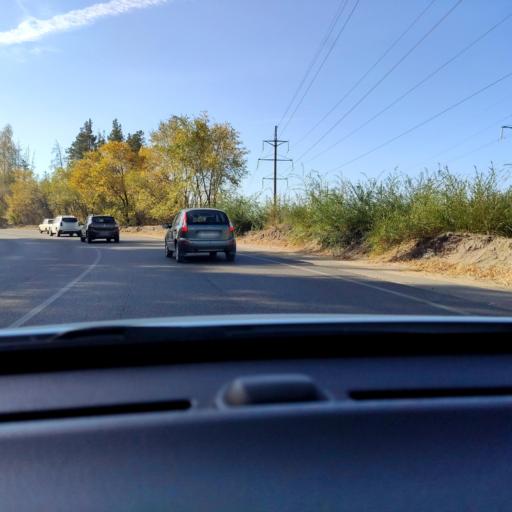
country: RU
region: Voronezj
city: Pridonskoy
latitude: 51.6788
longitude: 39.1123
